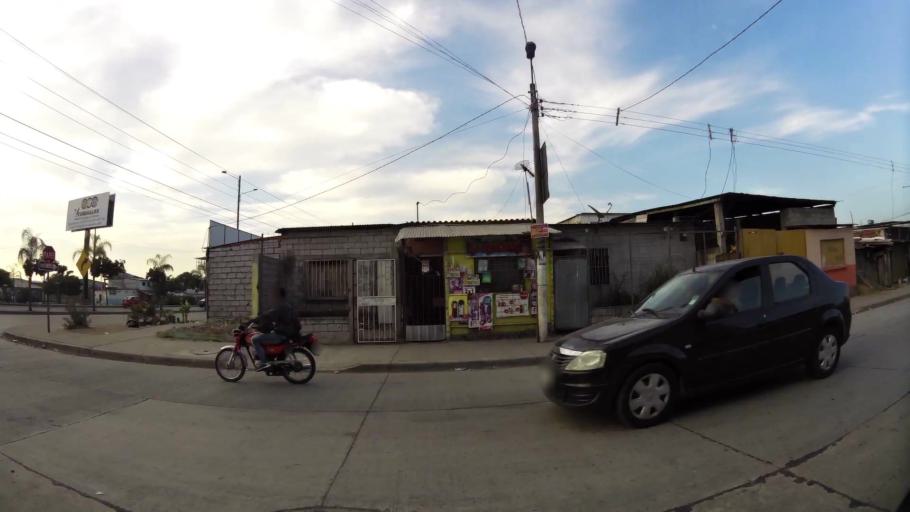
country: EC
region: Guayas
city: Eloy Alfaro
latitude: -2.0885
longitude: -79.8962
